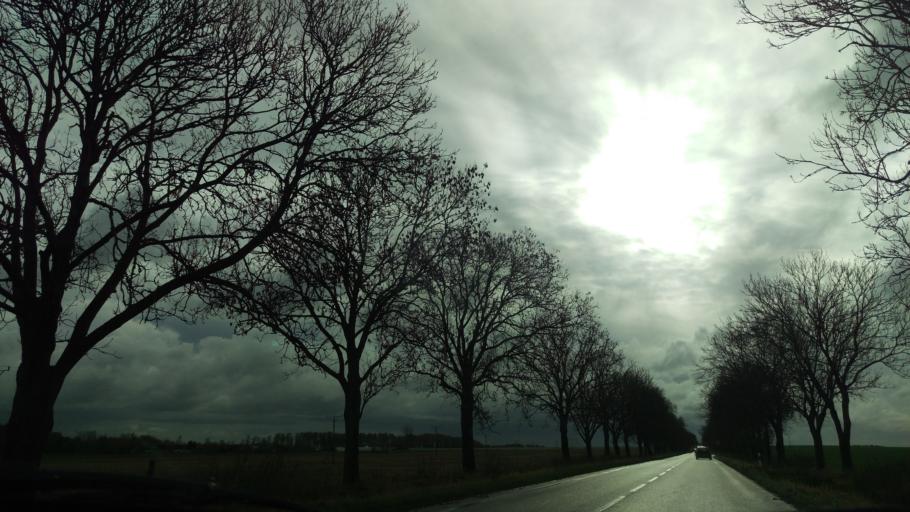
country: PL
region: West Pomeranian Voivodeship
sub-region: Powiat gryficki
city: Gryfice
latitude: 53.8785
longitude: 15.2128
